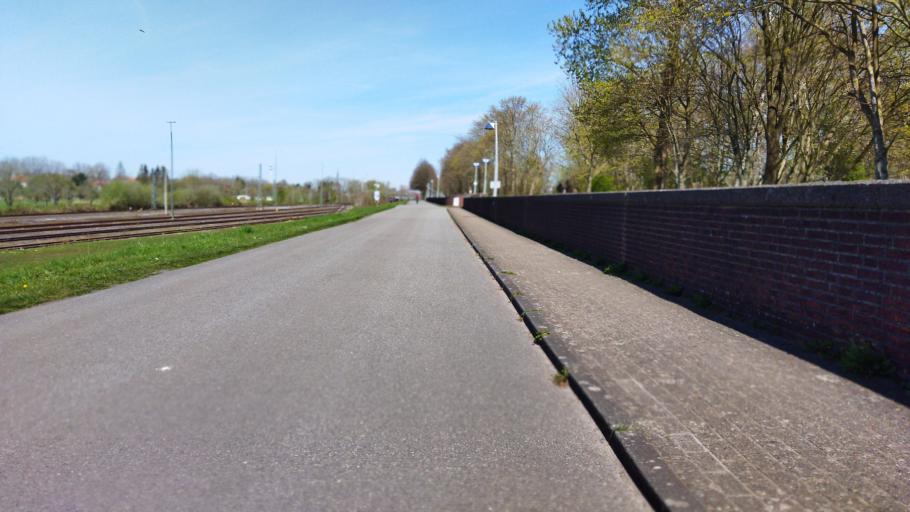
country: DE
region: Lower Saxony
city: Nordenham
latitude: 53.4699
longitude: 8.4786
